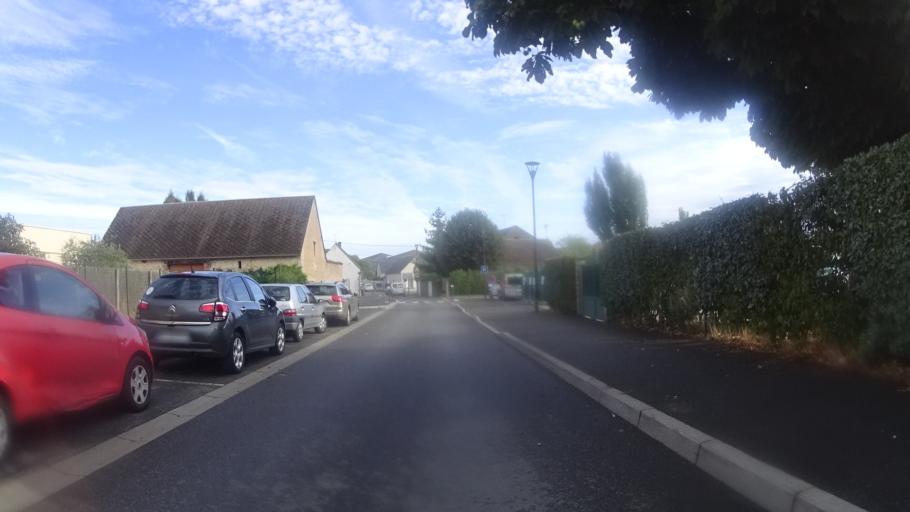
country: FR
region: Centre
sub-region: Departement du Loiret
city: Chateauneuf-sur-Loire
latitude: 47.8647
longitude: 2.2224
